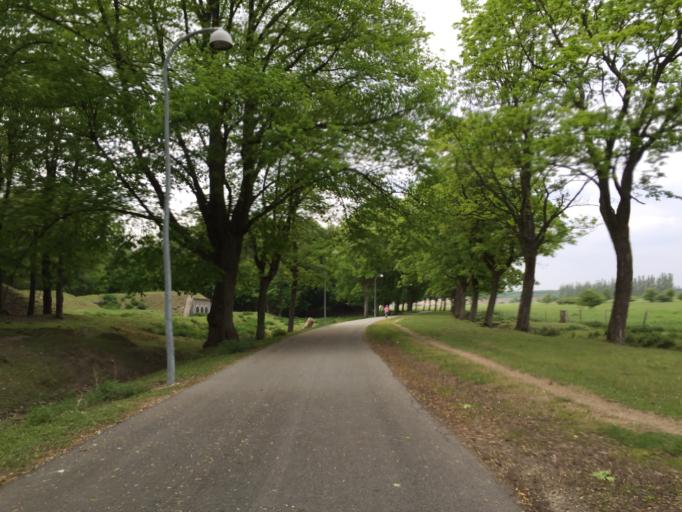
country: DK
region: Capital Region
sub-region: Brondby Kommune
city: Brondbyvester
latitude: 55.6343
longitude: 12.4331
